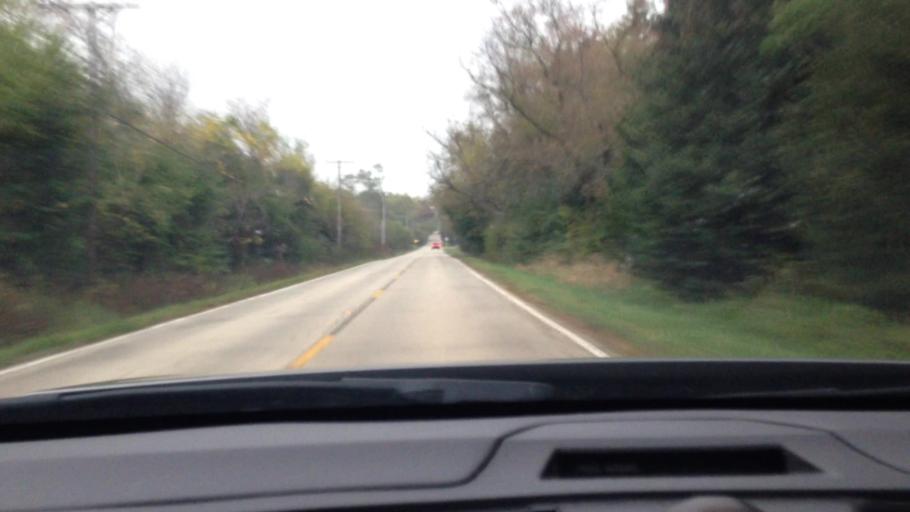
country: US
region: Illinois
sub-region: Cook County
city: Barrington Hills
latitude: 42.1017
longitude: -88.1947
